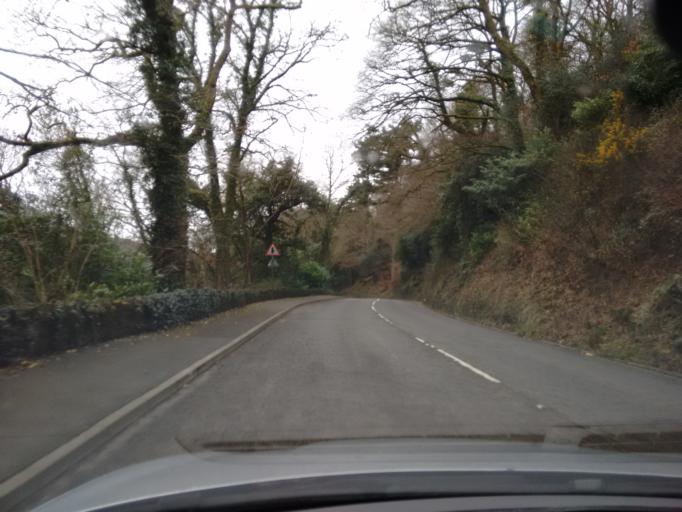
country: GB
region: England
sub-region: Devon
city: Okehampton
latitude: 50.7352
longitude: -4.0054
